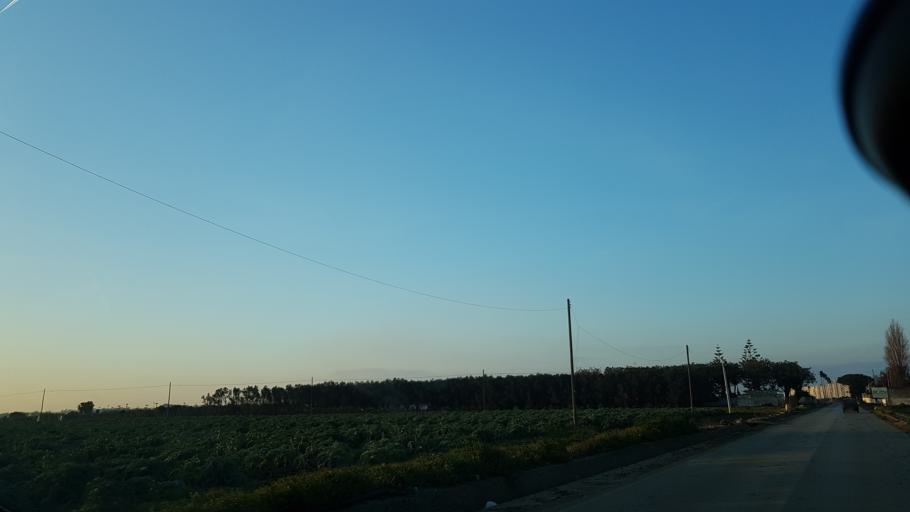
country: IT
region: Apulia
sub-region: Provincia di Brindisi
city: La Rosa
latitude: 40.6081
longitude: 17.9448
